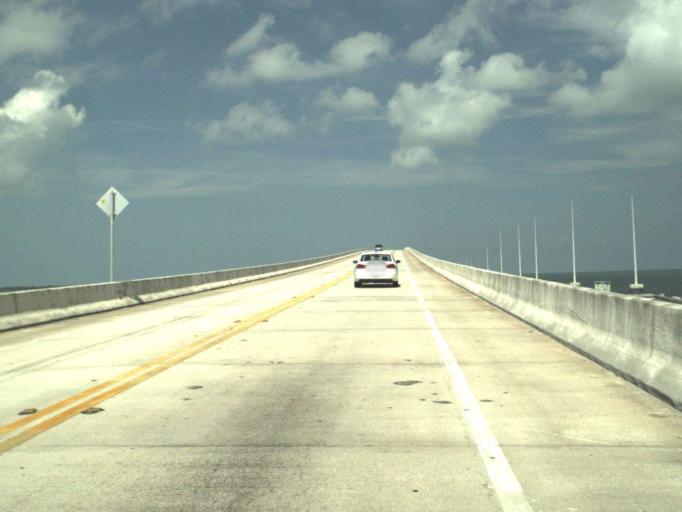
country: US
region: Florida
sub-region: Monroe County
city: Islamorada
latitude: 24.8364
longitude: -80.7662
